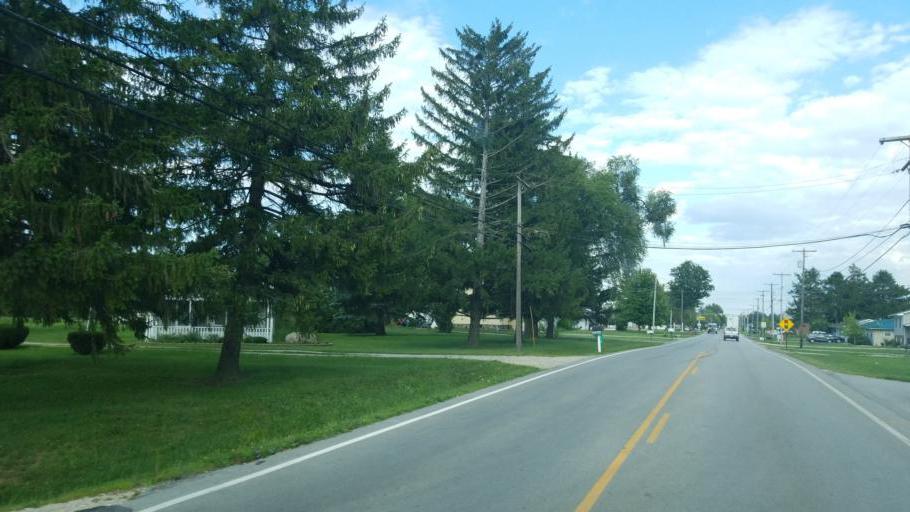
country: US
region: Ohio
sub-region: Sandusky County
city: Stony Prairie
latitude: 41.3421
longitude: -83.1497
